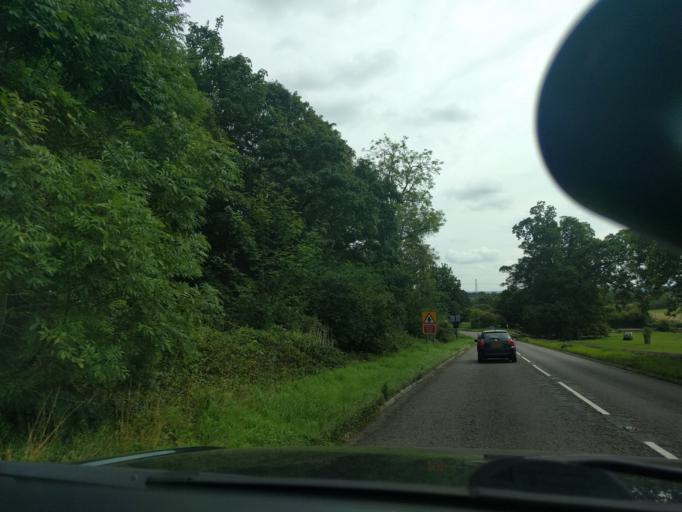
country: GB
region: England
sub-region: Wiltshire
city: Corsham
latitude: 51.4453
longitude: -2.1629
